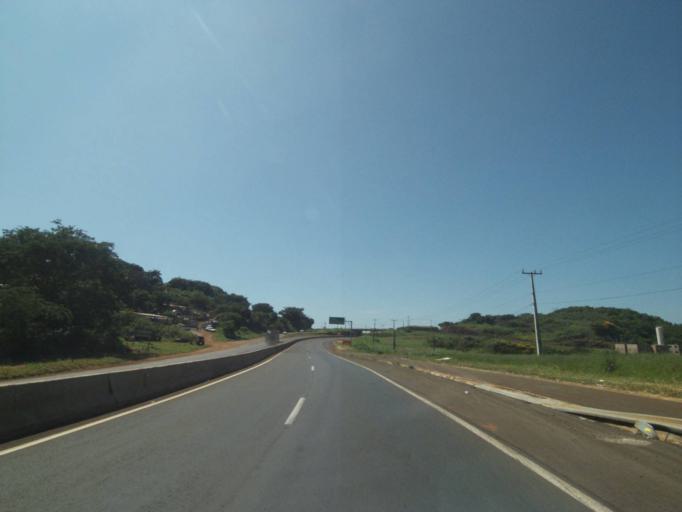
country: BR
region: Parana
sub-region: Londrina
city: Londrina
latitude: -23.3865
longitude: -51.1357
